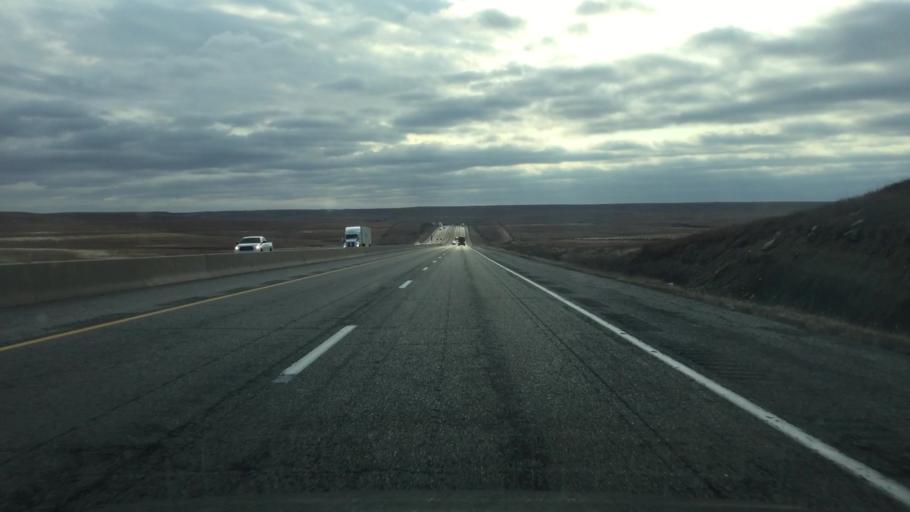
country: US
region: Kansas
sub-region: Chase County
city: Cottonwood Falls
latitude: 38.2645
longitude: -96.3829
